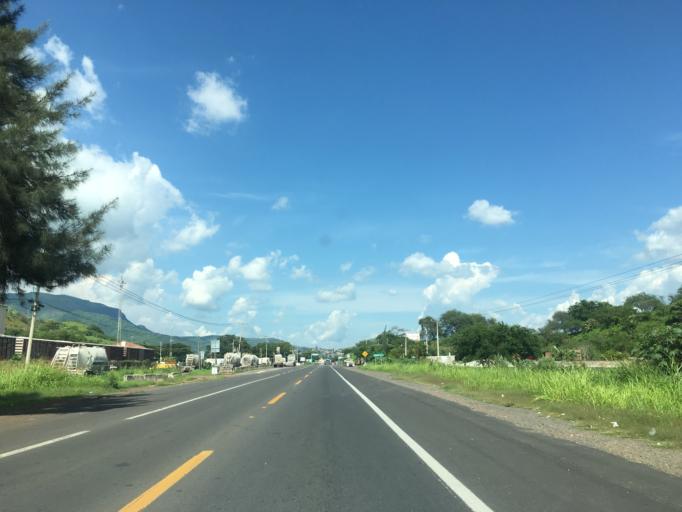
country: MX
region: Nayarit
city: Ixtlan del Rio
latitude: 21.0372
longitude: -104.3917
